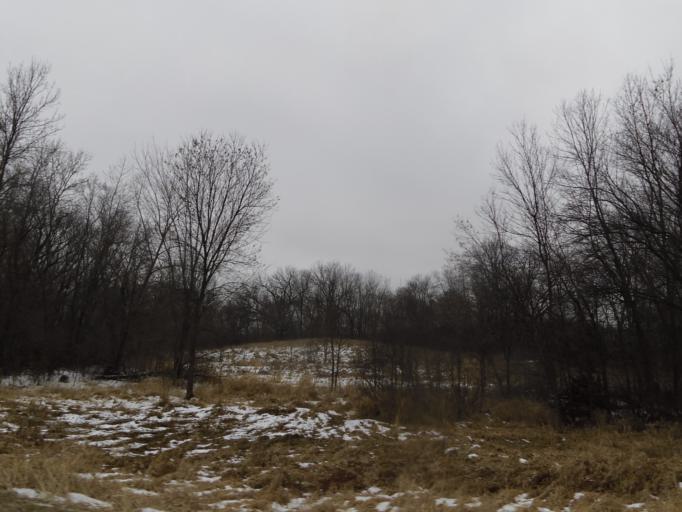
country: US
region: Minnesota
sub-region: Carver County
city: Watertown
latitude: 44.9726
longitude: -93.8496
